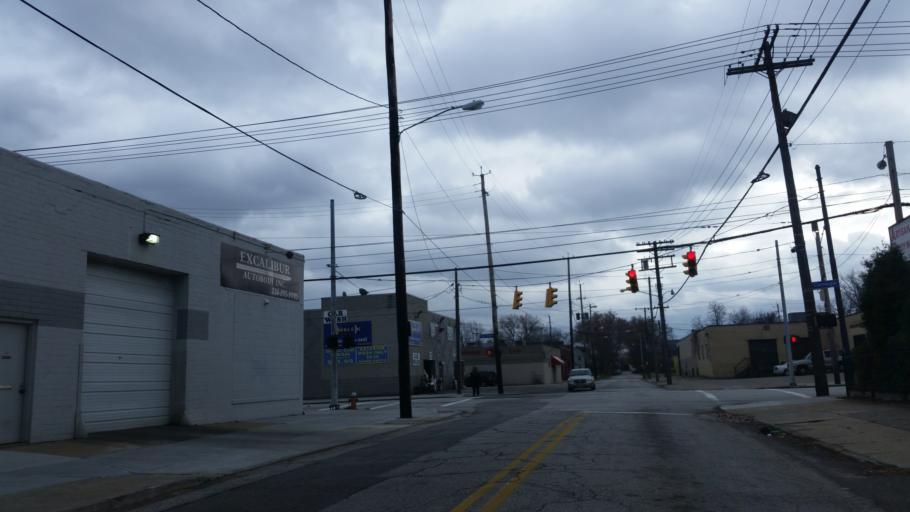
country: US
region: Ohio
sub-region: Cuyahoga County
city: Cleveland
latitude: 41.5008
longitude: -81.6623
